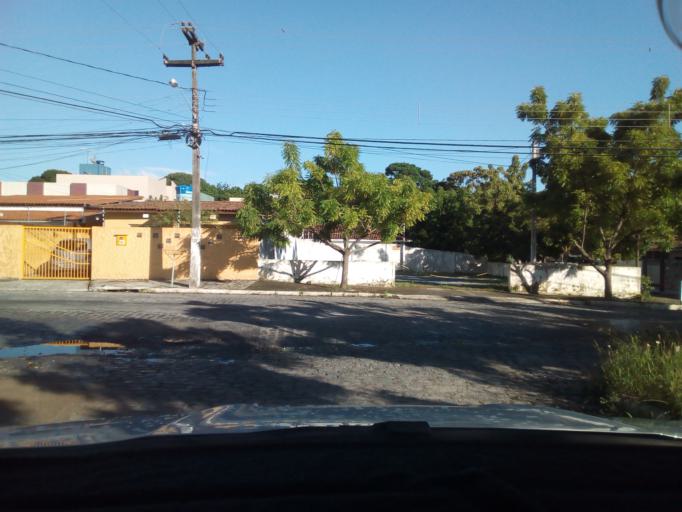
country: BR
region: Paraiba
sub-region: Joao Pessoa
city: Joao Pessoa
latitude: -7.1451
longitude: -34.8477
